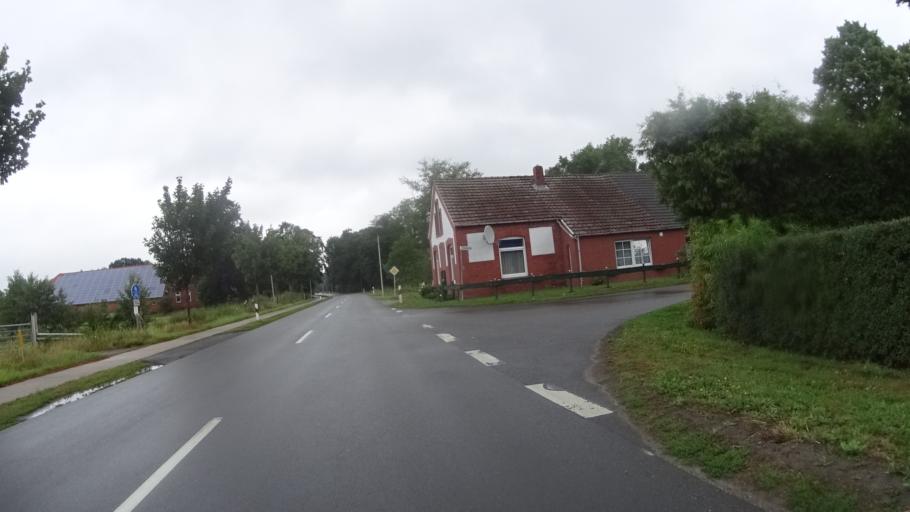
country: DE
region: Lower Saxony
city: Weener
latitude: 53.1819
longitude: 7.3116
